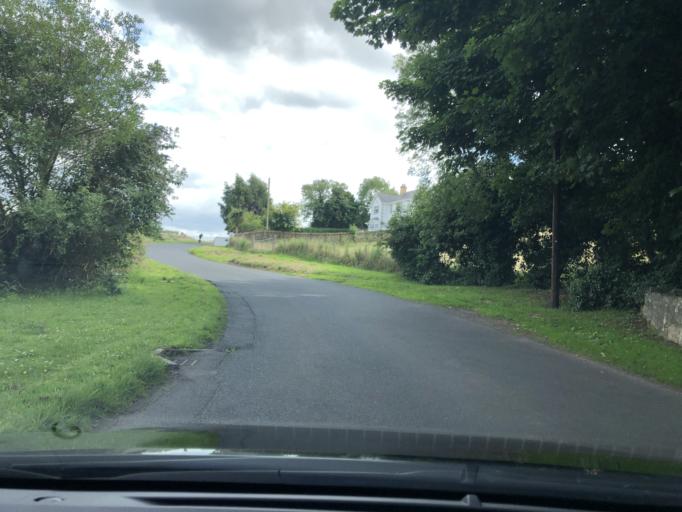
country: GB
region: Northern Ireland
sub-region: Ards District
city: Newtownards
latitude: 54.5855
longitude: -5.7133
